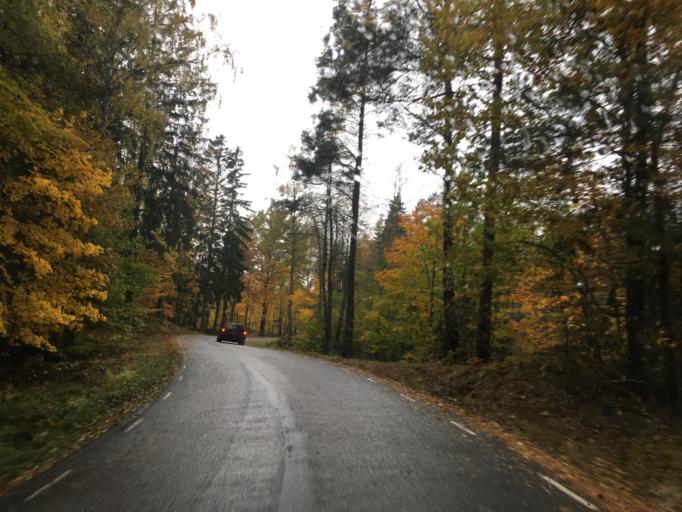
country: SE
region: Kronoberg
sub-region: Vaxjo Kommun
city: Ingelstad
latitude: 56.6154
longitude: 14.7188
